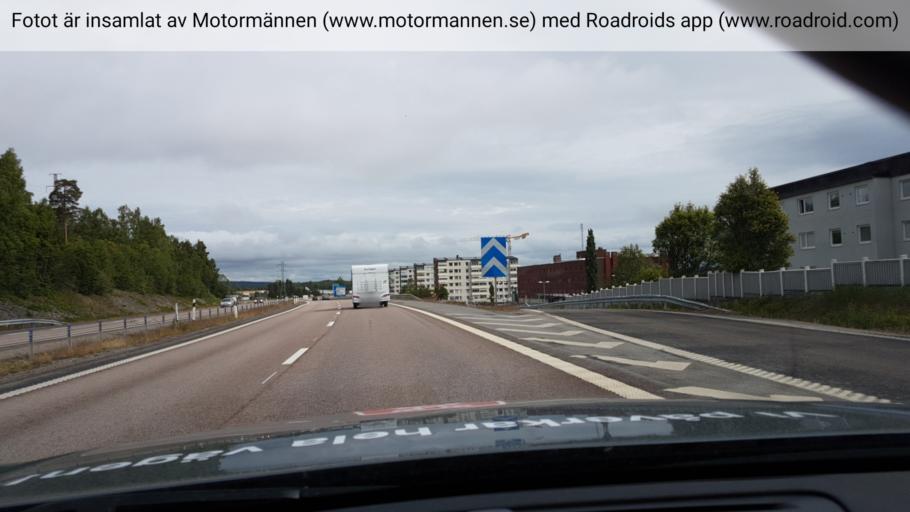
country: SE
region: Vaesternorrland
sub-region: Timra Kommun
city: Timra
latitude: 62.4852
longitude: 17.3212
